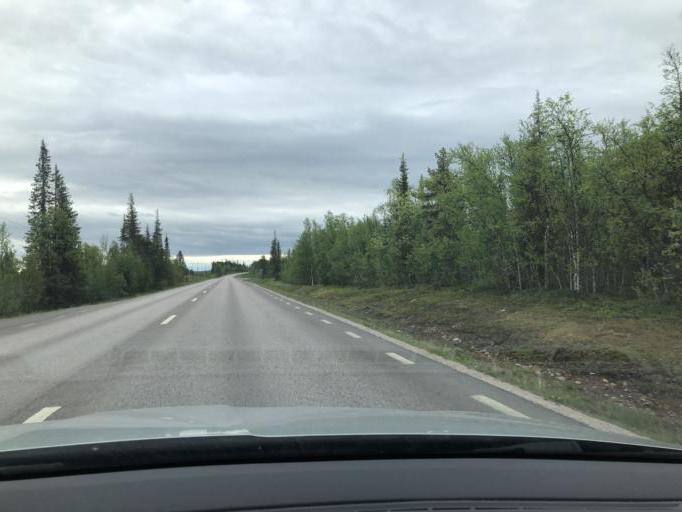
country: SE
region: Norrbotten
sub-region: Kiruna Kommun
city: Kiruna
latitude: 67.7646
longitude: 20.6249
